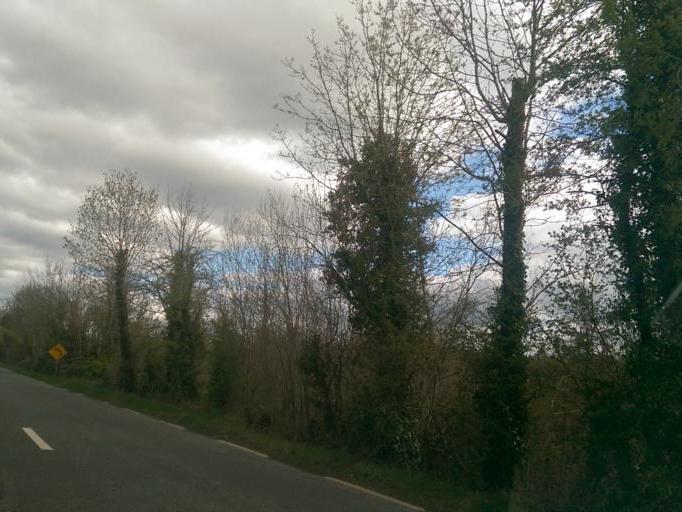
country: IE
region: Connaught
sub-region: County Galway
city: Ballinasloe
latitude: 53.4195
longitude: -8.3874
